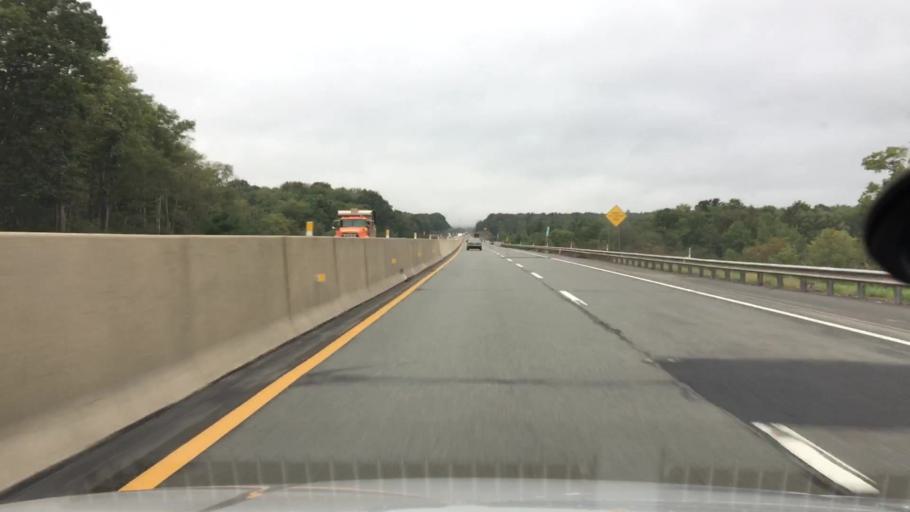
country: US
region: Pennsylvania
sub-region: Luzerne County
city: White Haven
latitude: 41.1110
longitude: -75.7562
